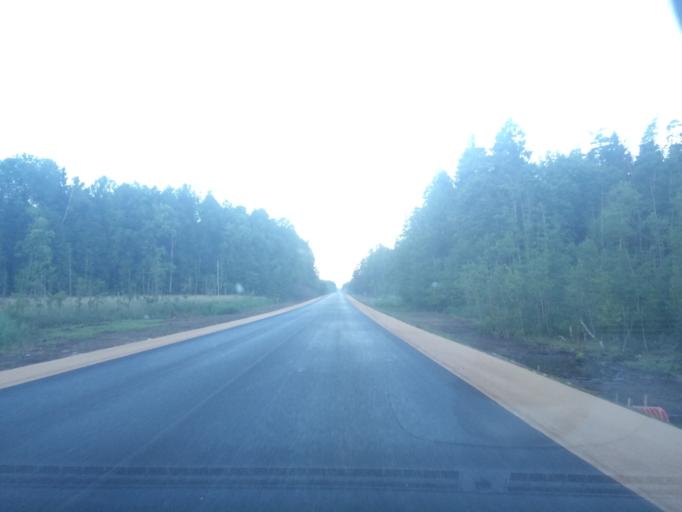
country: LT
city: Zarasai
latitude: 55.7679
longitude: 26.3415
